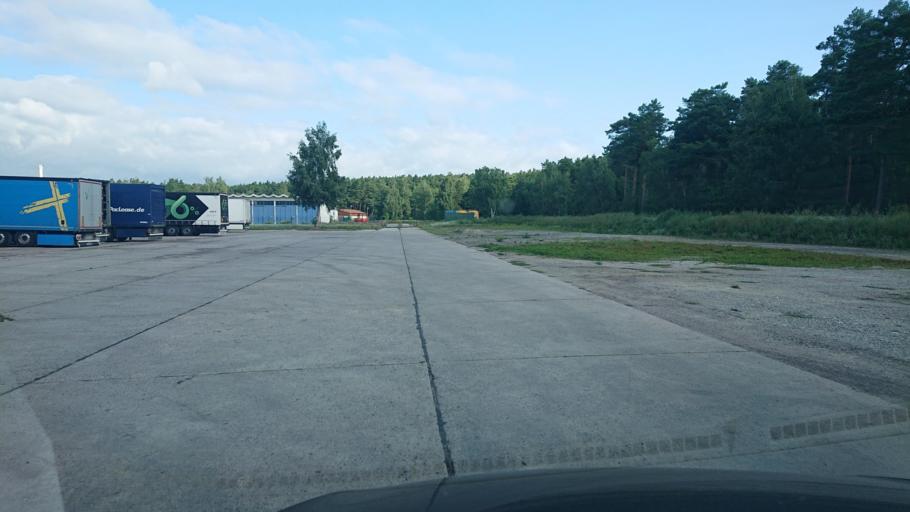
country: DE
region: Brandenburg
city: Gross Kreutz
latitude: 52.3588
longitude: 12.7777
